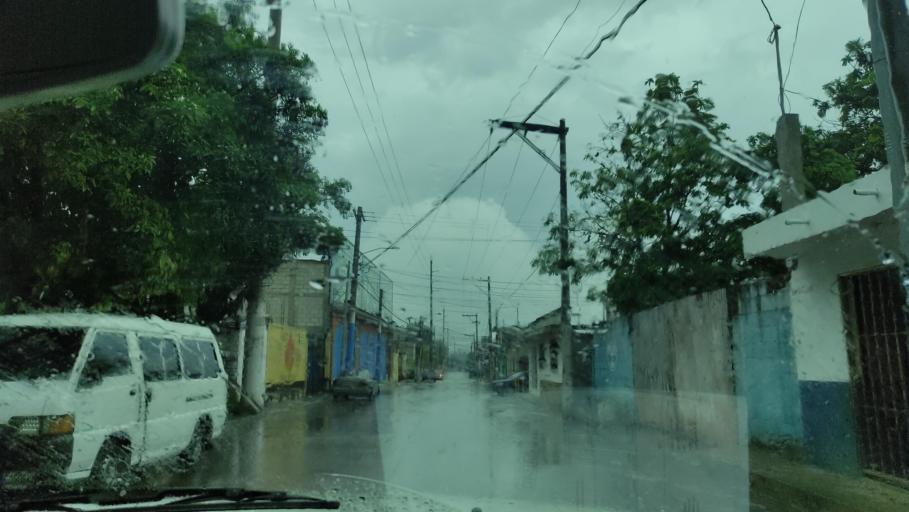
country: GT
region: Guatemala
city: Petapa
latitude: 14.5022
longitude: -90.5594
